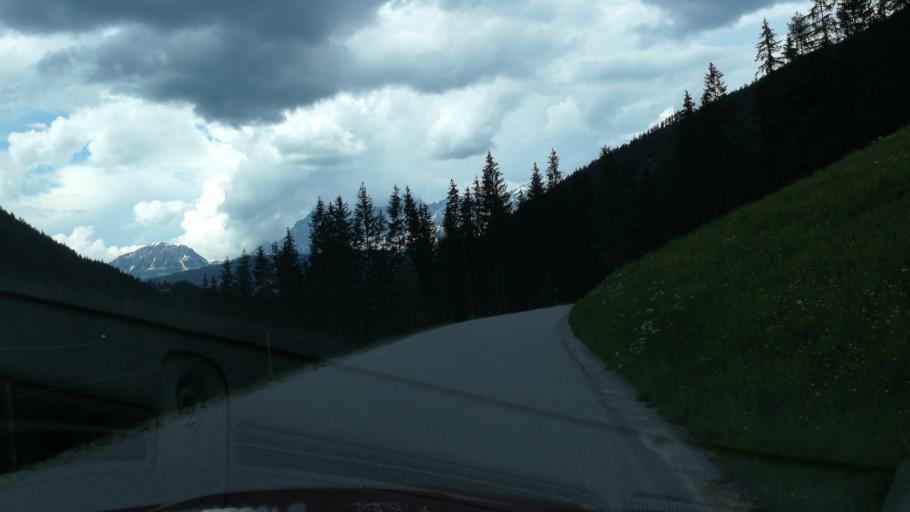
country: AT
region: Styria
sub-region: Politischer Bezirk Liezen
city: Schladming
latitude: 47.3598
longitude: 13.6193
